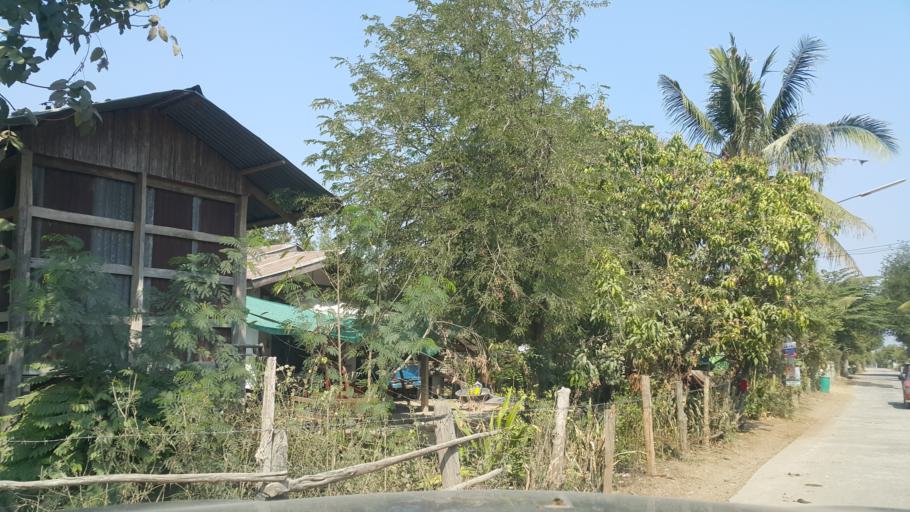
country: TH
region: Buriram
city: Ban Dan
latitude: 15.1325
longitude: 103.3456
